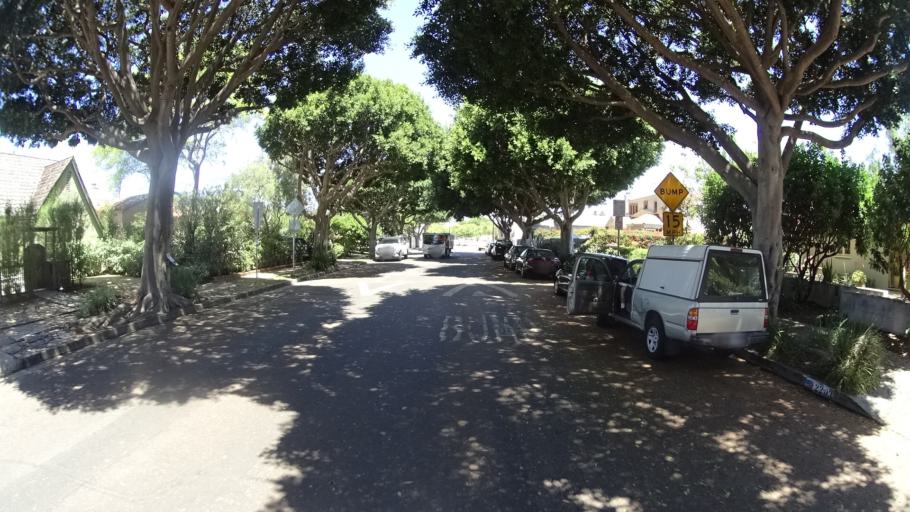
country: US
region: California
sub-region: Los Angeles County
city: Santa Monica
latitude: 34.0197
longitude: -118.4668
